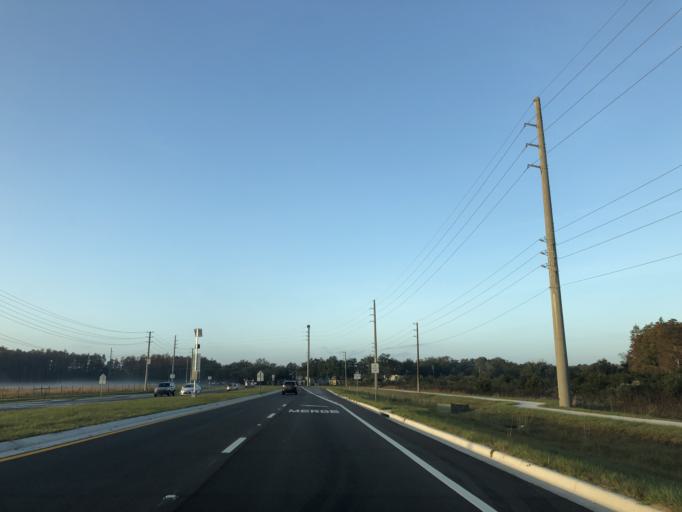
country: US
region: Florida
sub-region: Osceola County
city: Kissimmee
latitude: 28.3194
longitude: -81.4429
